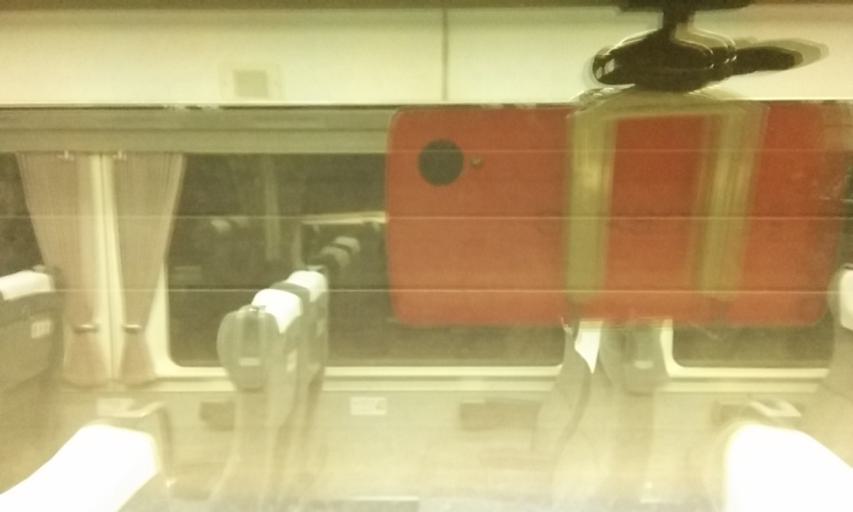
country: JP
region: Nagano
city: Nagano-shi
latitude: 36.4807
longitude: 138.0967
